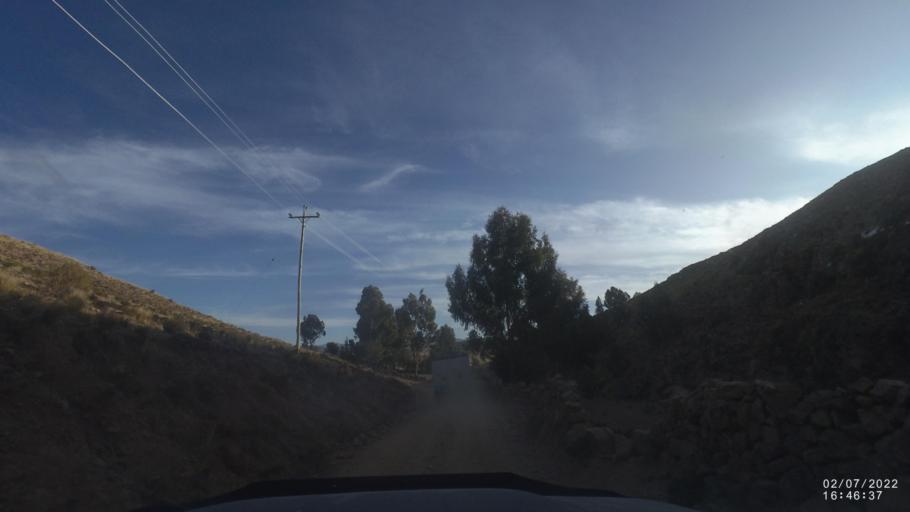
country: BO
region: Cochabamba
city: Irpa Irpa
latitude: -17.9776
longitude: -66.5133
